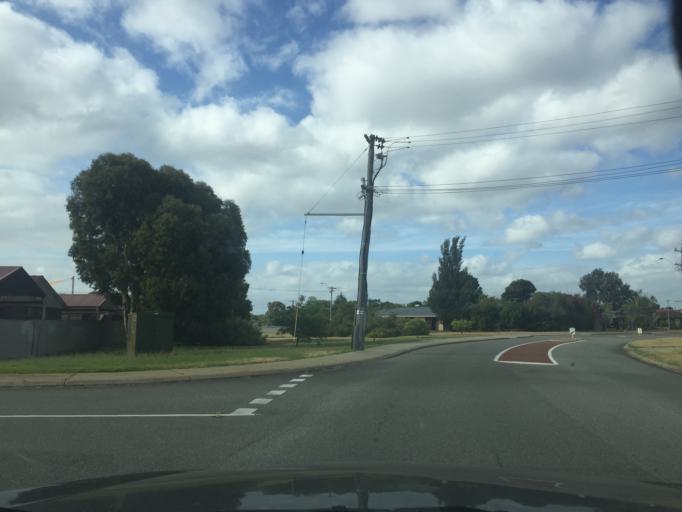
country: AU
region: Western Australia
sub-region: Canning
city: Ferndale
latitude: -32.0439
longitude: 115.9098
